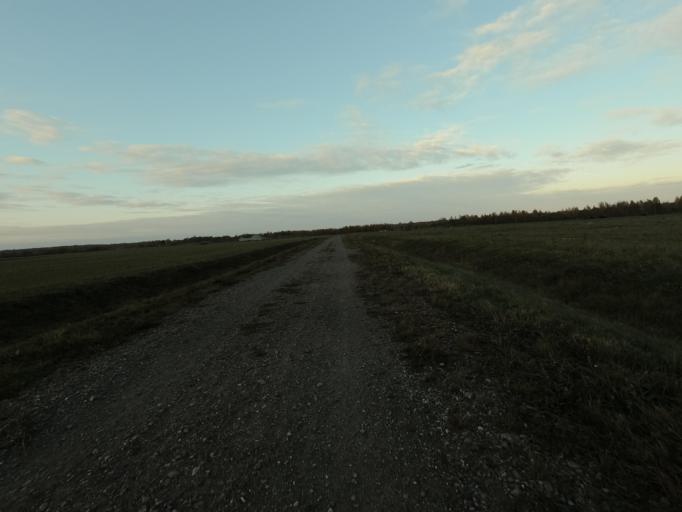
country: RU
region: Leningrad
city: Mga
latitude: 59.7867
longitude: 31.1989
